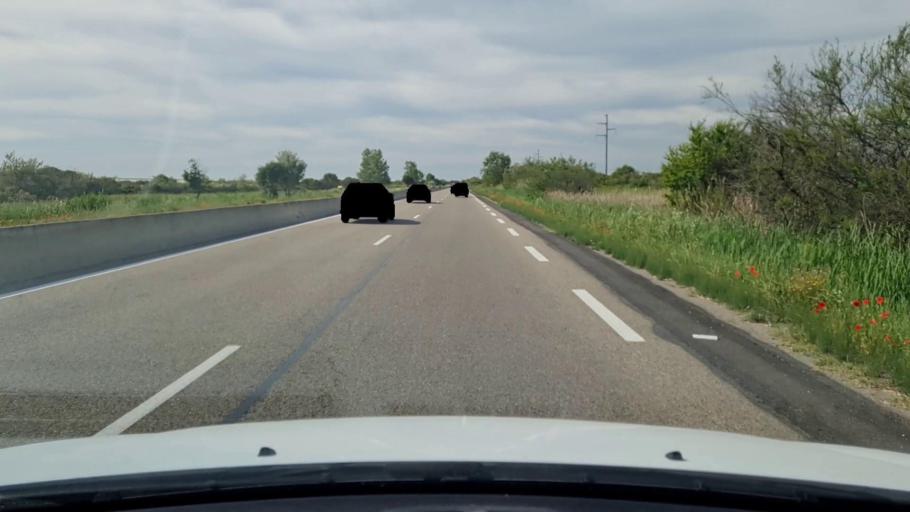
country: FR
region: Languedoc-Roussillon
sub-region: Departement du Gard
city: Aigues-Mortes
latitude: 43.6095
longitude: 4.1932
